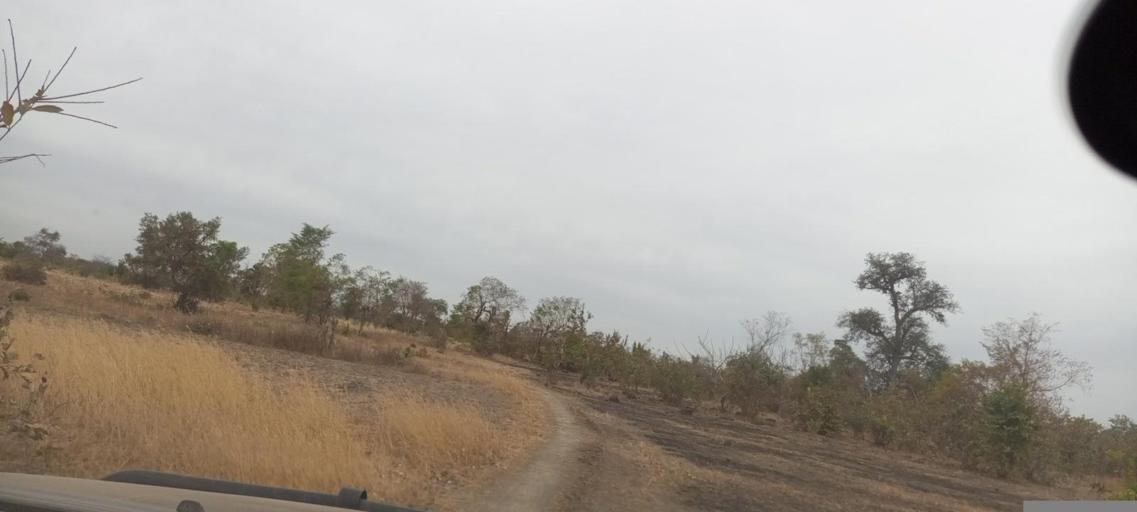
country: ML
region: Koulikoro
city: Kati
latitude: 12.7516
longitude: -8.3607
